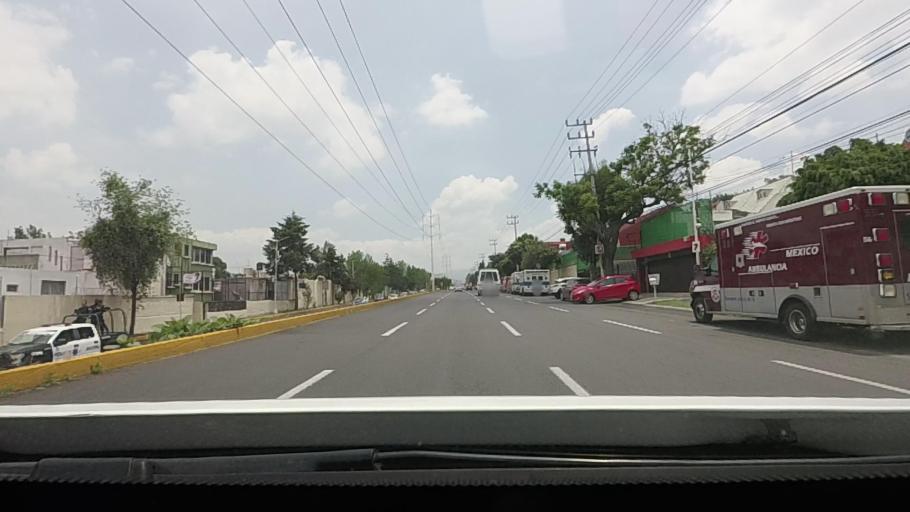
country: MX
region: Mexico
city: Naucalpan de Juarez
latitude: 19.5089
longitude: -99.2492
